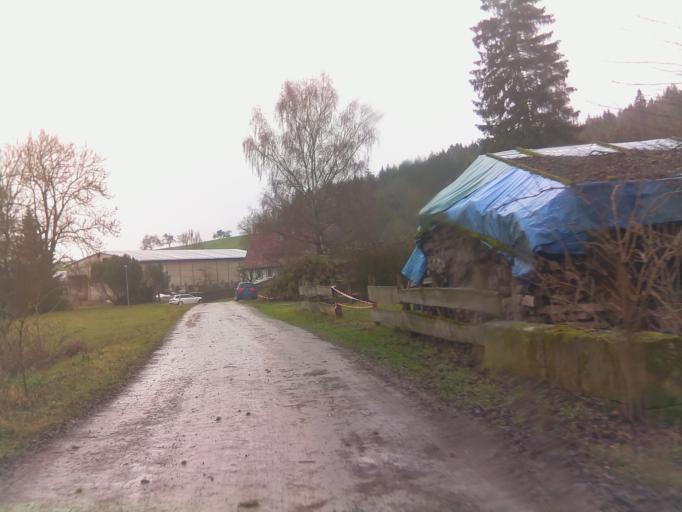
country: DE
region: Thuringia
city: Gleichamberg
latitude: 50.3971
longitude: 10.6184
